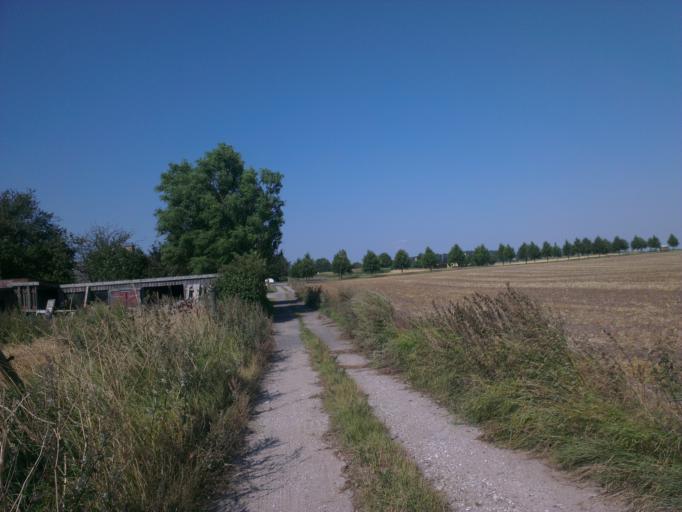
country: DK
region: Capital Region
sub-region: Frederikssund Kommune
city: Skibby
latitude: 55.7653
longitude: 11.9460
